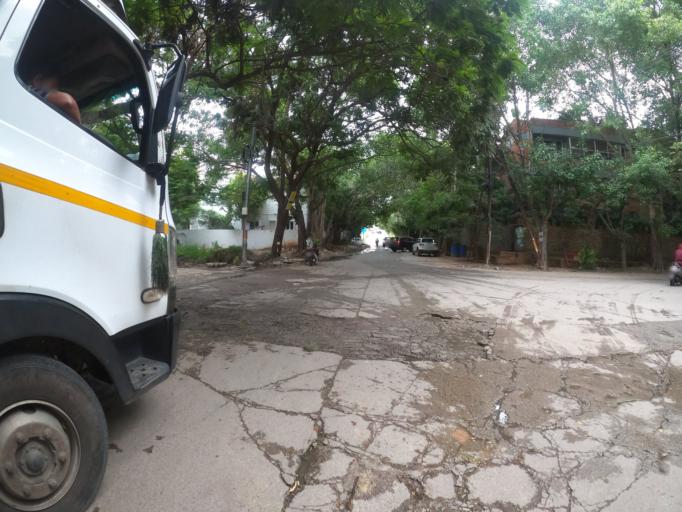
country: IN
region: Telangana
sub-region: Rangareddi
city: Kukatpalli
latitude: 17.4249
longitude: 78.4002
